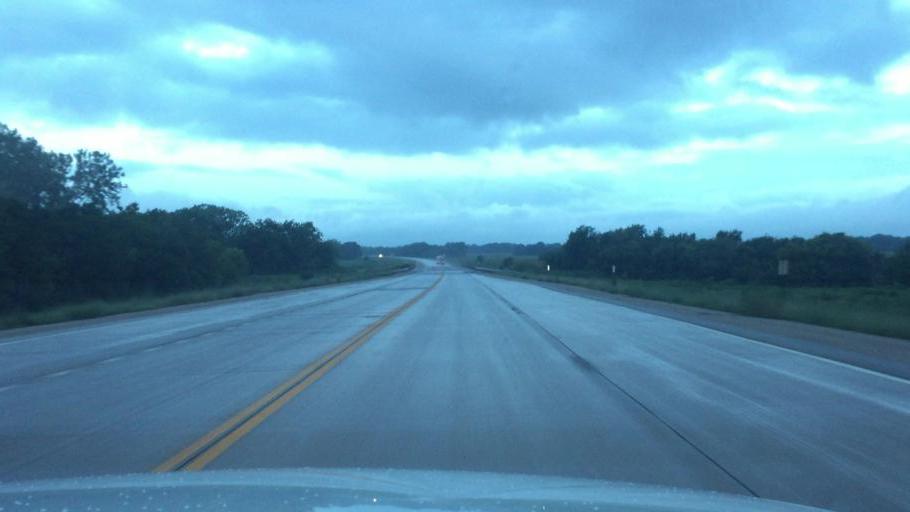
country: US
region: Kansas
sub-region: Neosho County
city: Chanute
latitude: 37.7416
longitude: -95.4399
